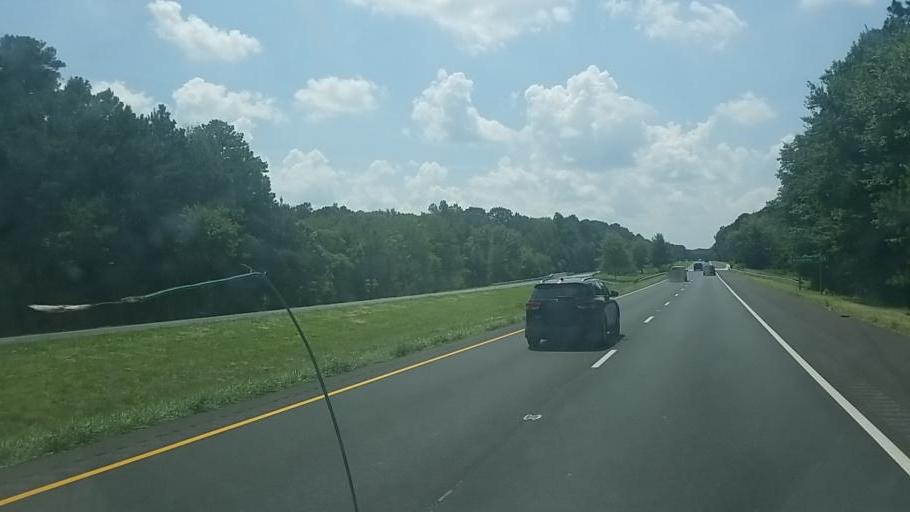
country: US
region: Maryland
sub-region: Wicomico County
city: Salisbury
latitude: 38.3533
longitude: -75.5417
